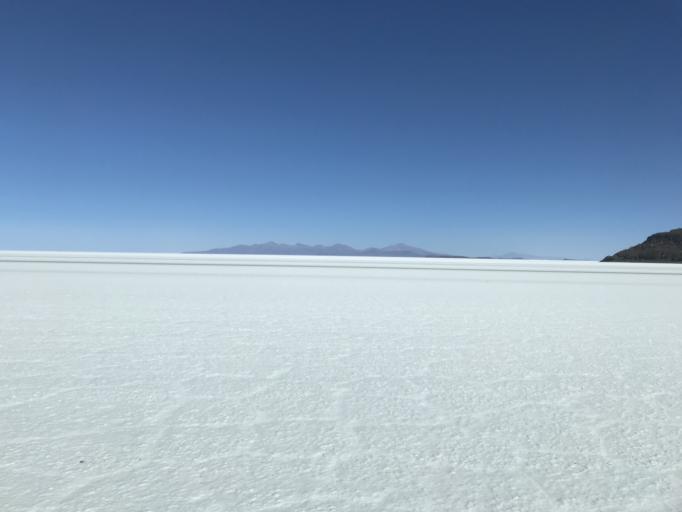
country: BO
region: Potosi
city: Colchani
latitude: -20.2384
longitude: -67.6188
